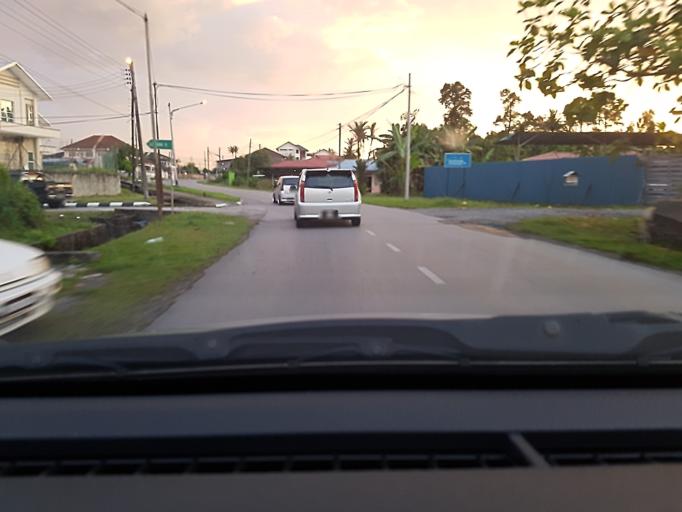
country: MY
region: Sarawak
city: Kuching
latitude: 1.4907
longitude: 110.3223
